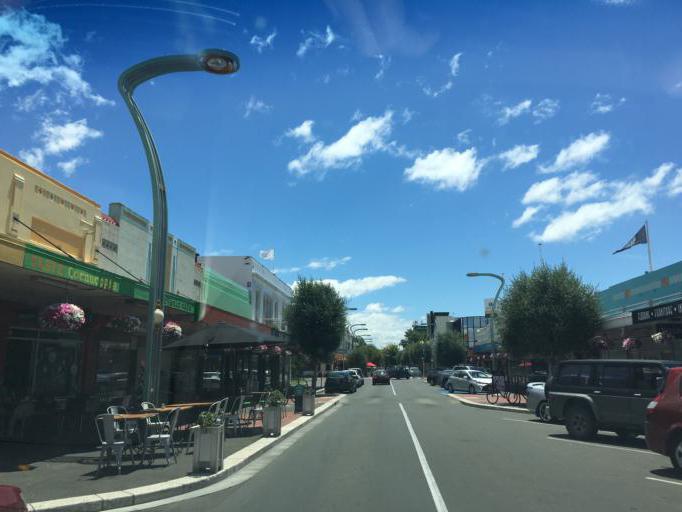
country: NZ
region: Hawke's Bay
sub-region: Hastings District
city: Hastings
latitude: -39.6435
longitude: 176.8449
